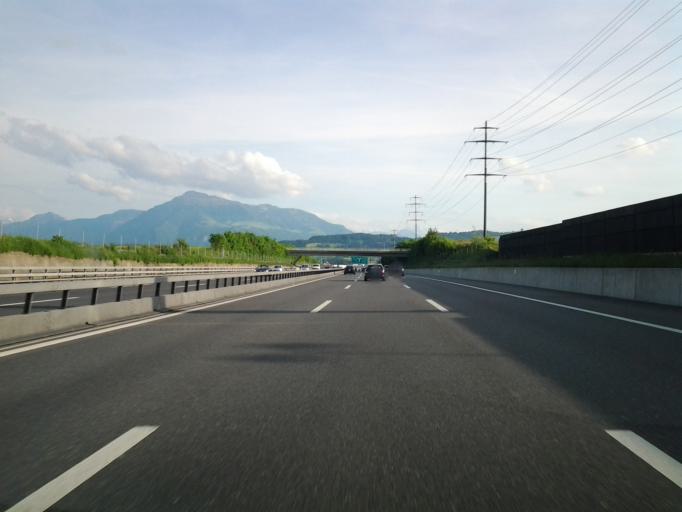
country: CH
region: Zug
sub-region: Zug
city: Hunenberg
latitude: 47.1715
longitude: 8.4320
